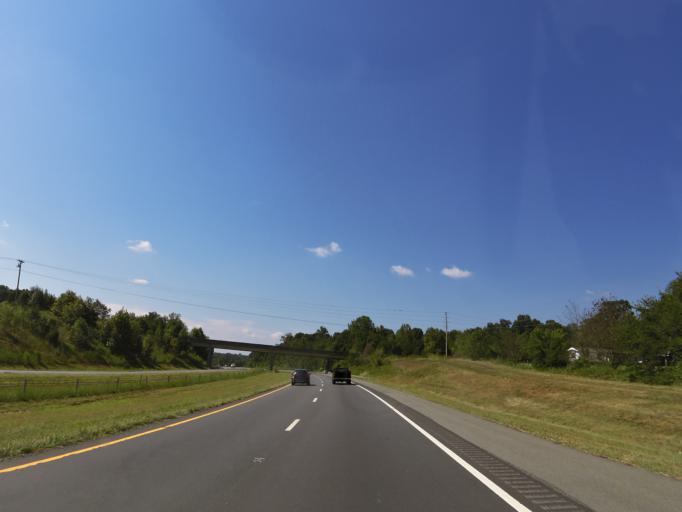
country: US
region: North Carolina
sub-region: Catawba County
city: Maiden
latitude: 35.5527
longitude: -81.2402
